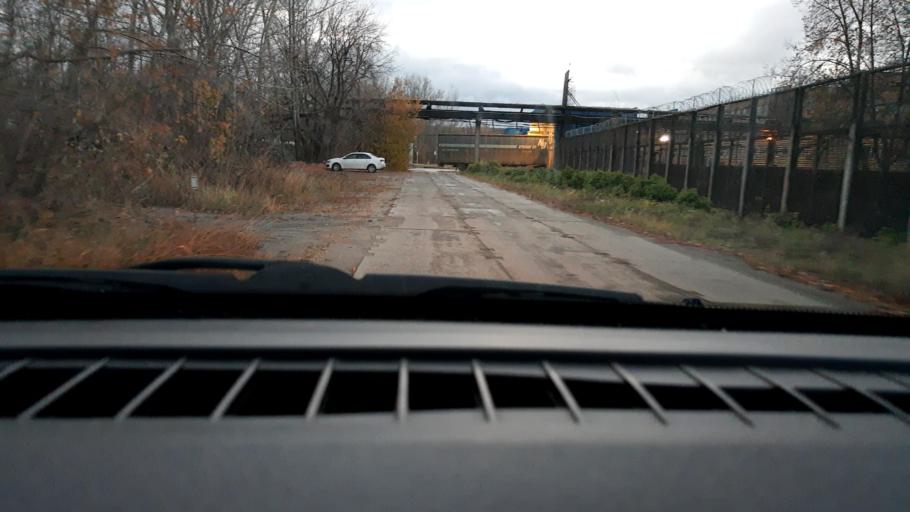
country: RU
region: Nizjnij Novgorod
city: Nizhniy Novgorod
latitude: 56.2383
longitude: 43.9022
